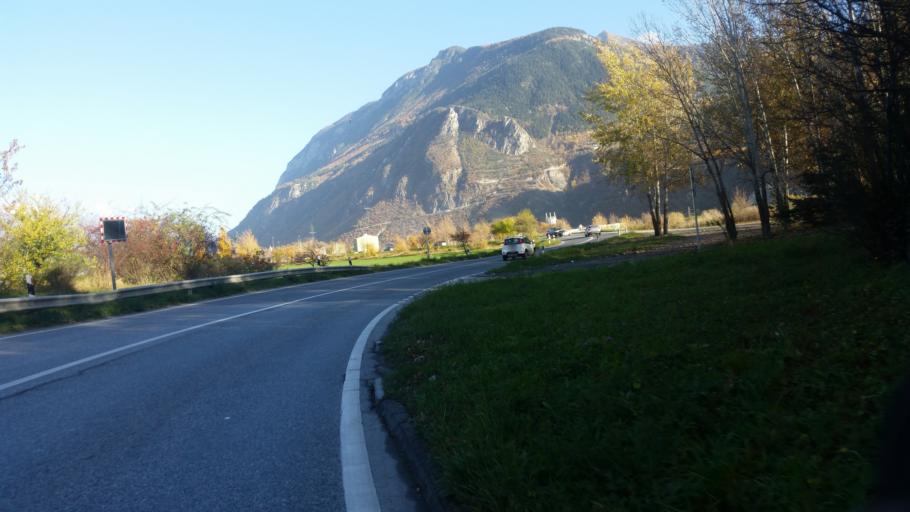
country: CH
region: Valais
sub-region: Sierre District
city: Chalais
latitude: 46.2825
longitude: 7.5188
